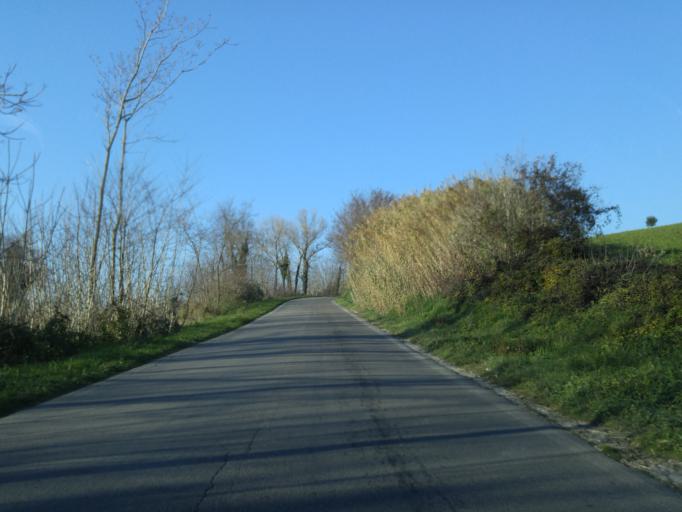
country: IT
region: The Marches
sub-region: Provincia di Pesaro e Urbino
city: Montefelcino
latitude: 43.7182
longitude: 12.8460
